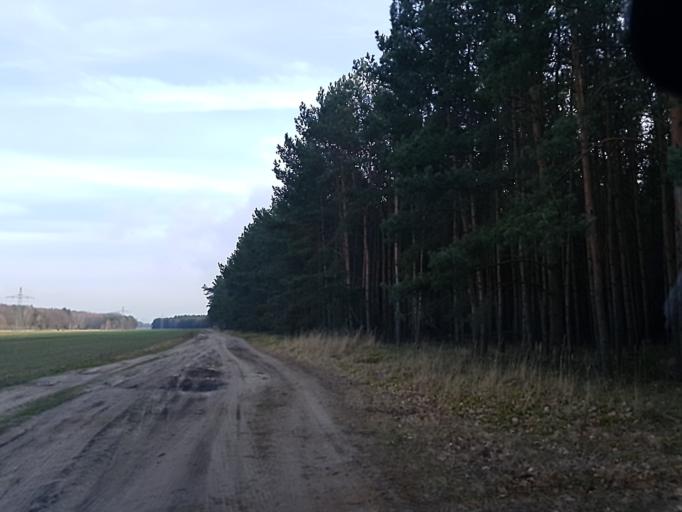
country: DE
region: Brandenburg
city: Wollin
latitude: 52.2659
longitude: 12.5051
